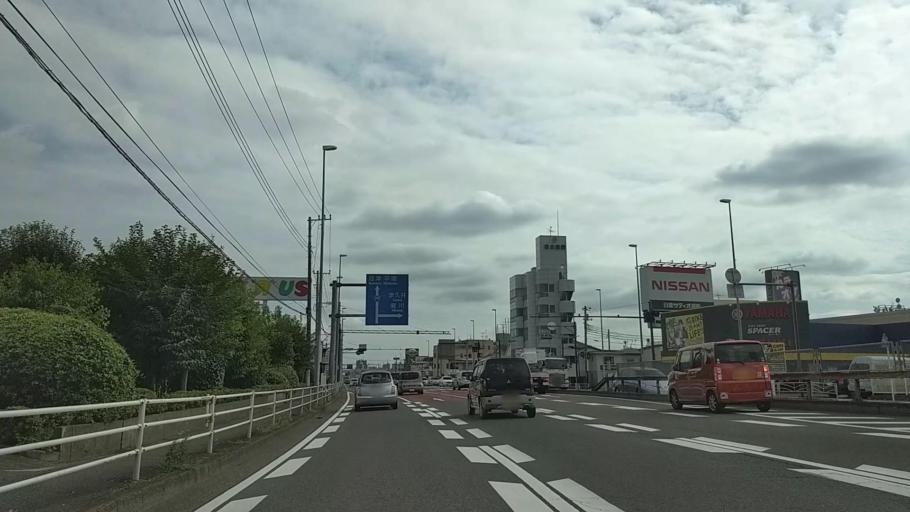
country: JP
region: Kanagawa
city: Atsugi
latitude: 35.4616
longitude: 139.3598
